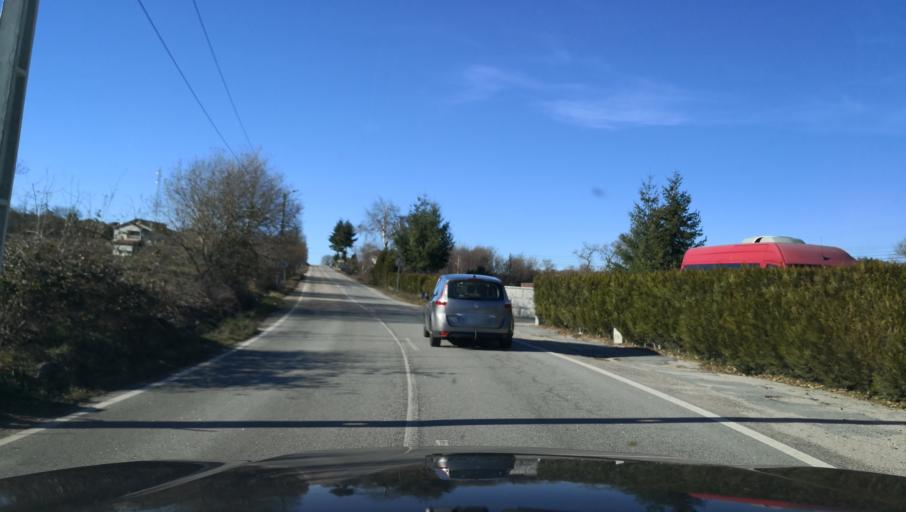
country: PT
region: Vila Real
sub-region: Vila Pouca de Aguiar
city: Vila Pouca de Aguiar
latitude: 41.4996
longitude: -7.6842
